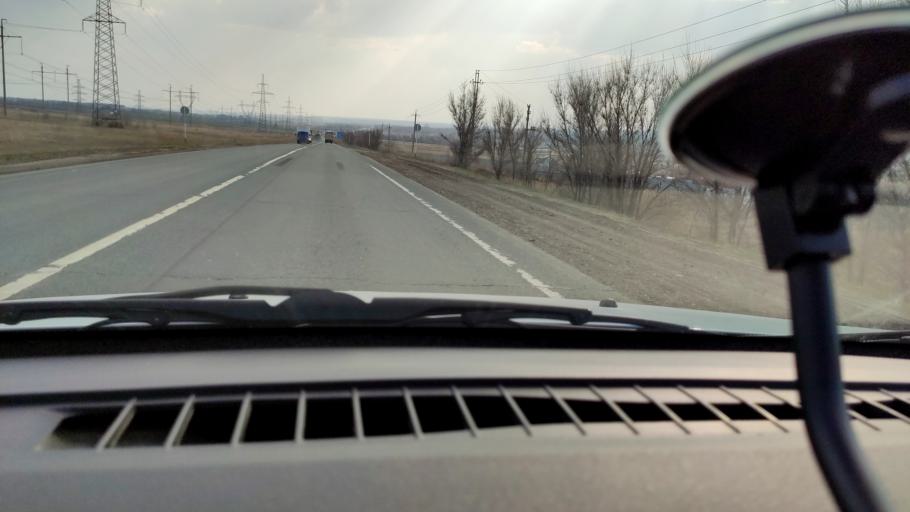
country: RU
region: Samara
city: Dubovyy Umet
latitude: 53.0691
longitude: 50.3810
